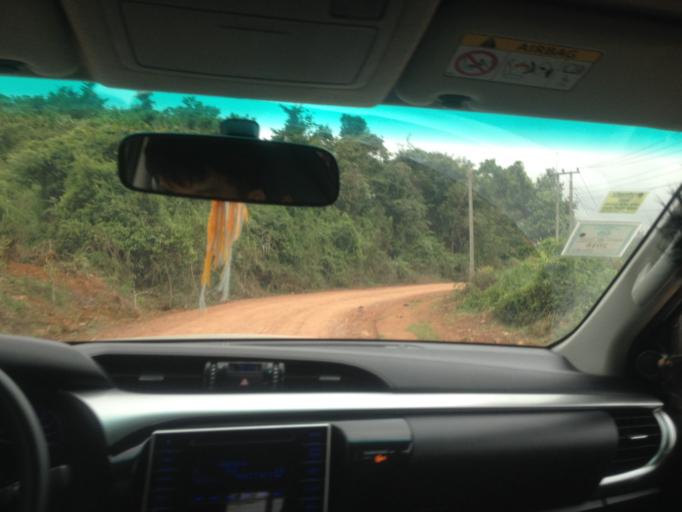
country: TH
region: Nan
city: Chaloem Phra Kiat
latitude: 19.9655
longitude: 101.1385
